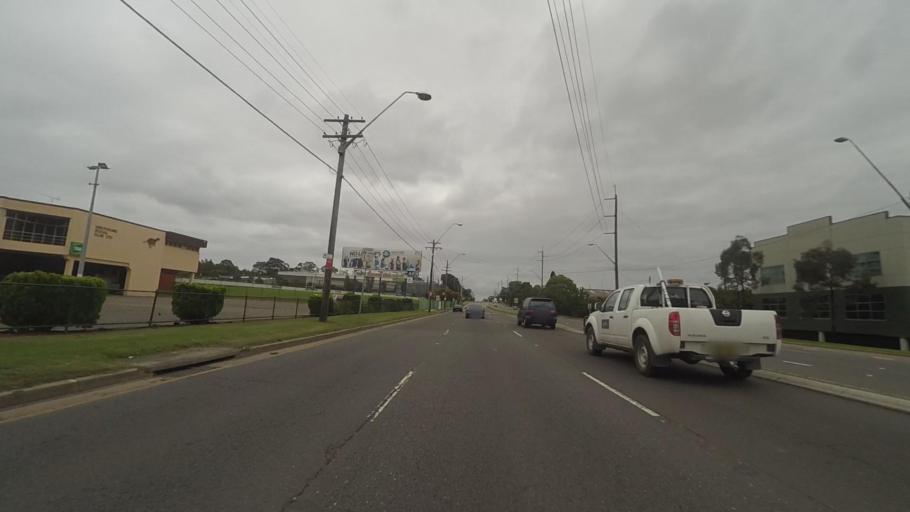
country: AU
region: New South Wales
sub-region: Bankstown
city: Bankstown
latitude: -33.8967
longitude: 151.0376
